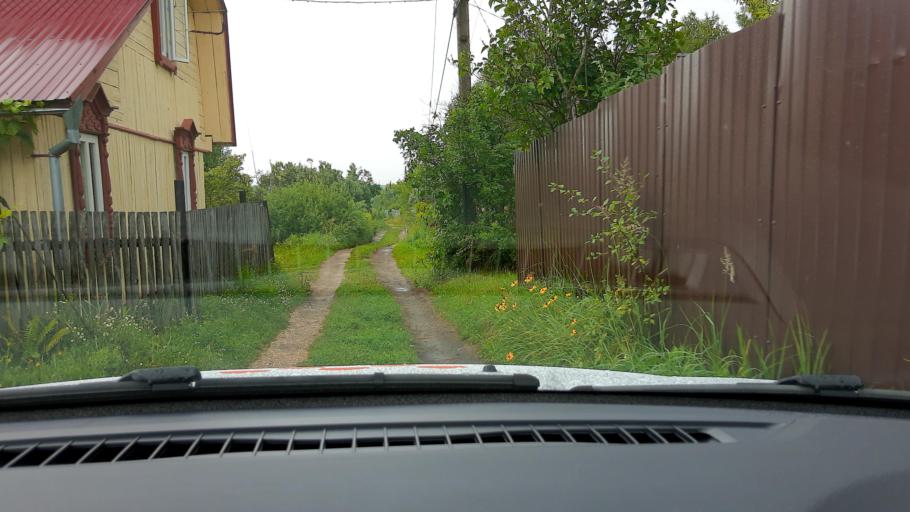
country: RU
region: Nizjnij Novgorod
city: Surovatikha
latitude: 55.9297
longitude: 43.9248
